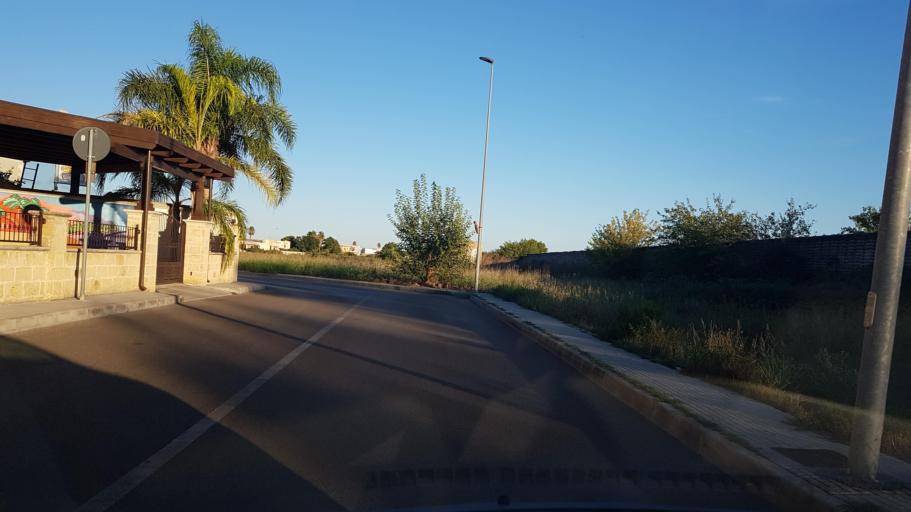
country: IT
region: Apulia
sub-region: Provincia di Lecce
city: Guagnano
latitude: 40.3973
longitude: 17.9485
